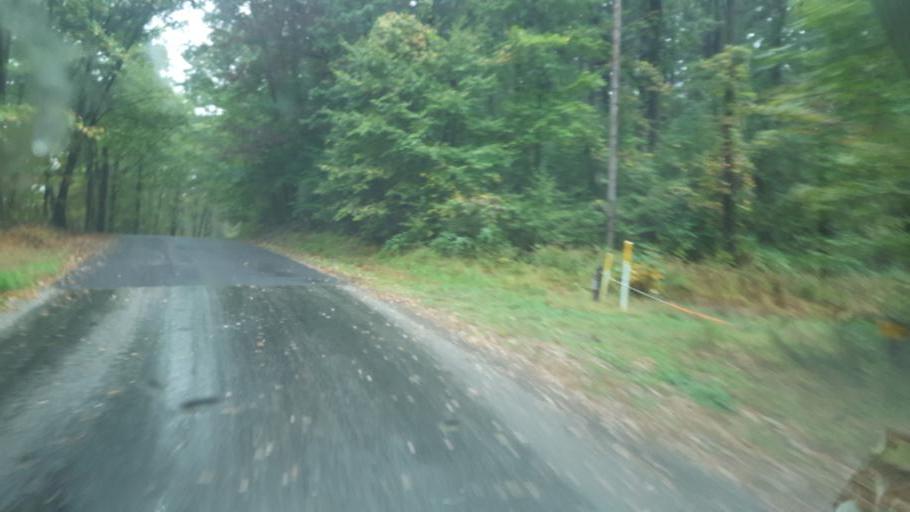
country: US
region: Ohio
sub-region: Ashland County
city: Loudonville
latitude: 40.6021
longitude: -82.3125
